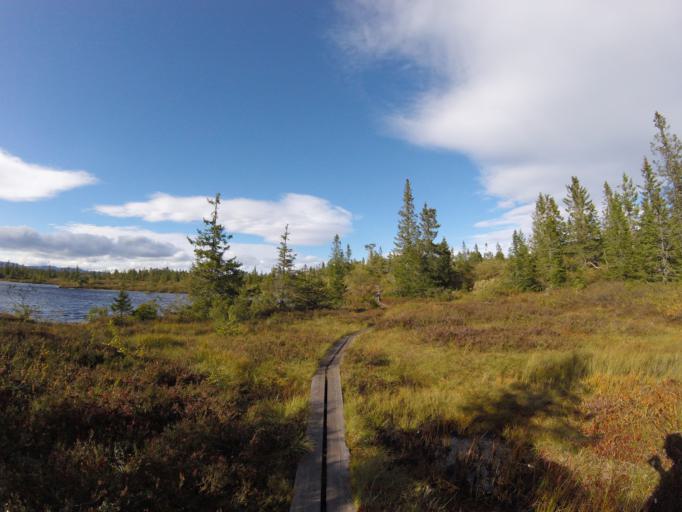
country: NO
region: Buskerud
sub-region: Flesberg
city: Lampeland
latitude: 59.7666
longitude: 9.4121
